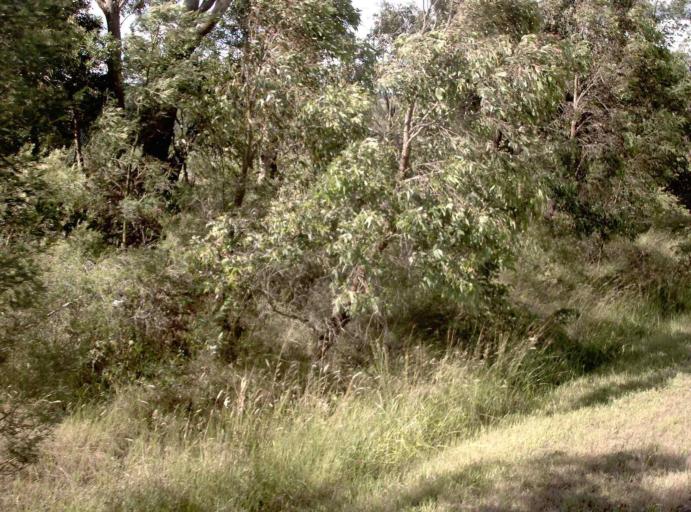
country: AU
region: Victoria
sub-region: Latrobe
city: Morwell
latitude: -38.1694
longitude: 146.4107
